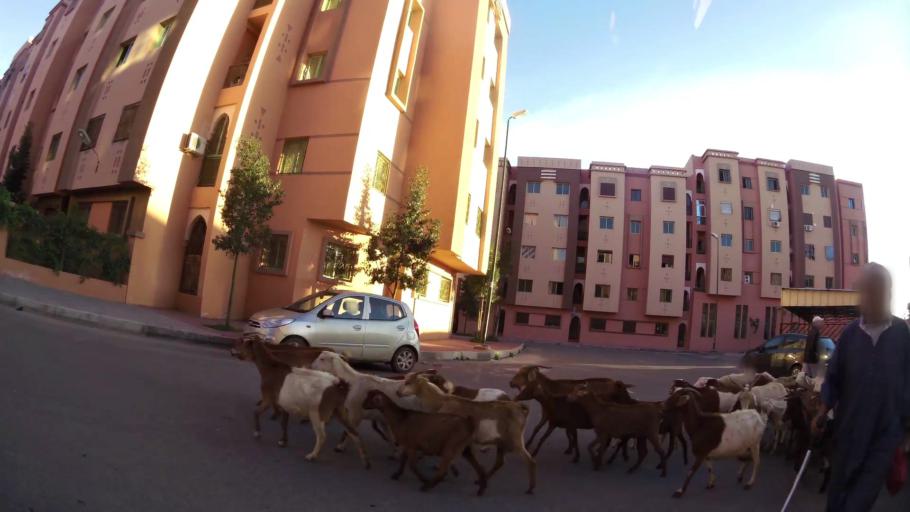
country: MA
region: Marrakech-Tensift-Al Haouz
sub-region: Marrakech
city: Marrakesh
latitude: 31.6504
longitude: -8.0377
